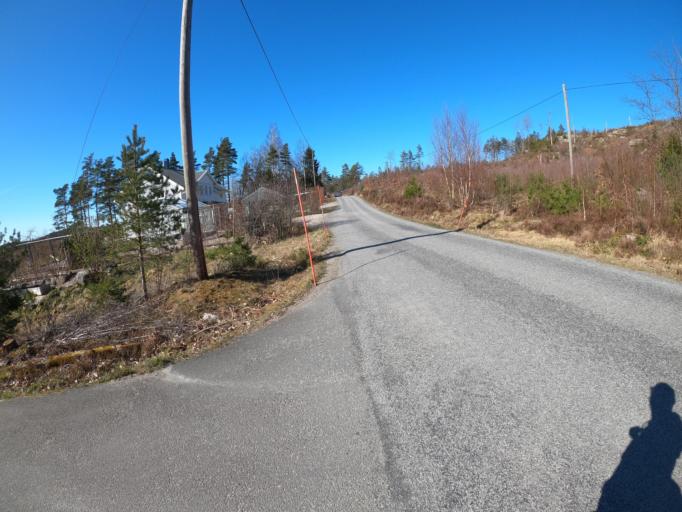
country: SE
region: Vaestra Goetaland
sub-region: Harryda Kommun
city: Molnlycke
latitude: 57.6342
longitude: 12.1157
